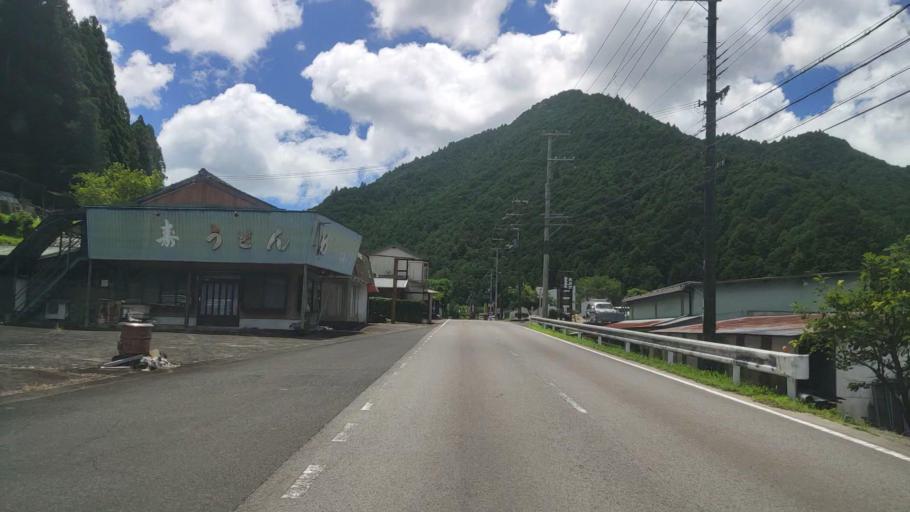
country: JP
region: Mie
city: Owase
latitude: 33.9652
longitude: 136.0609
